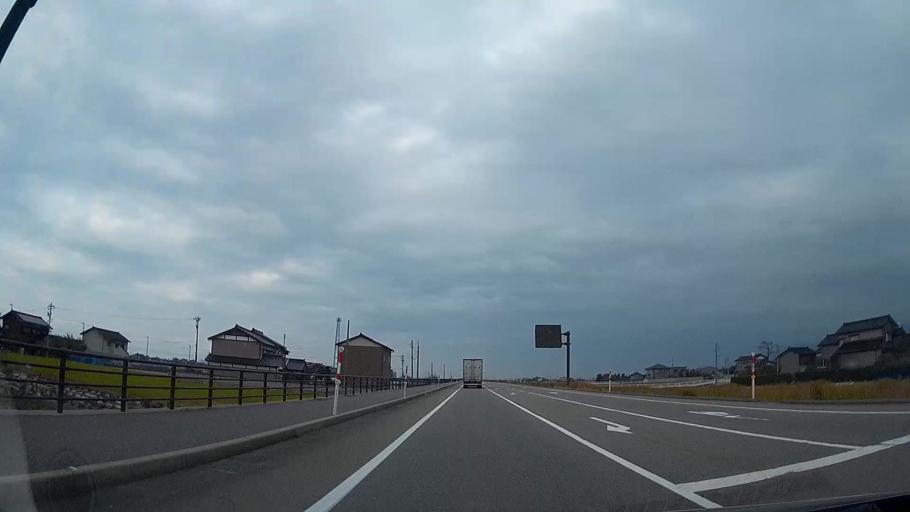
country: JP
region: Toyama
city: Nyuzen
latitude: 36.9212
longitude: 137.4670
